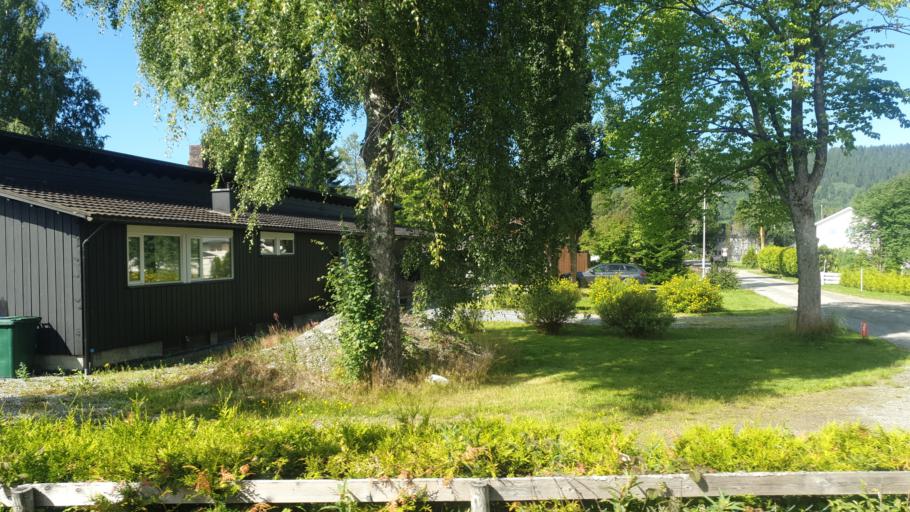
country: NO
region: Sor-Trondelag
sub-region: Orkdal
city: Orkanger
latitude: 63.2878
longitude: 9.8428
